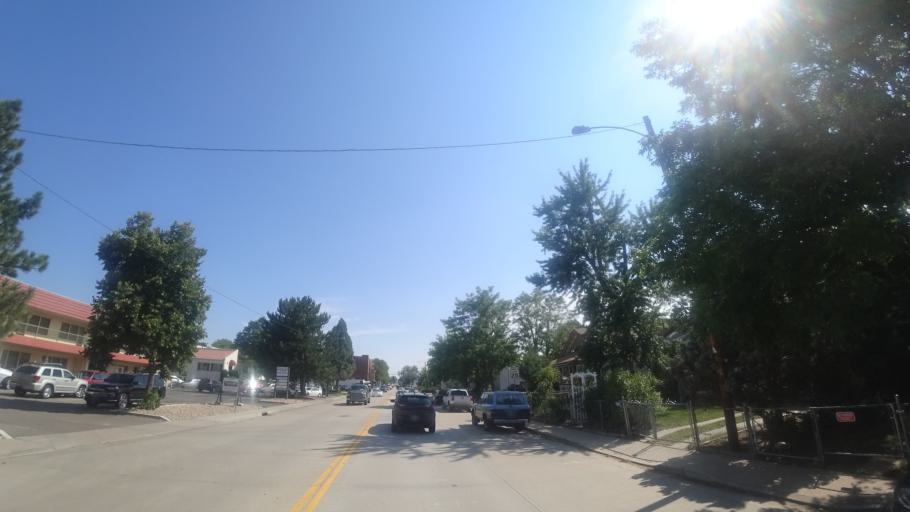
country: US
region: Colorado
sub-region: Arapahoe County
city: Littleton
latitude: 39.6162
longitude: -105.0162
